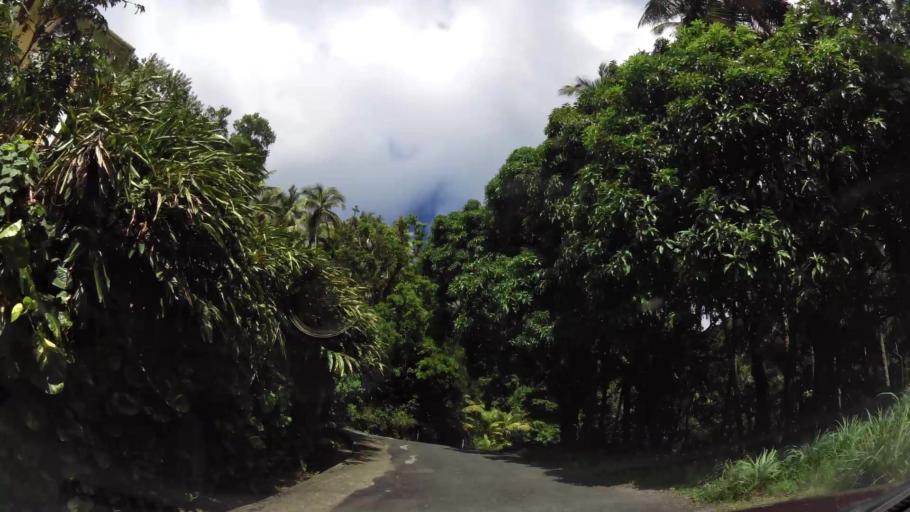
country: DM
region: Saint John
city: Portsmouth
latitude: 15.6083
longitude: -61.4546
